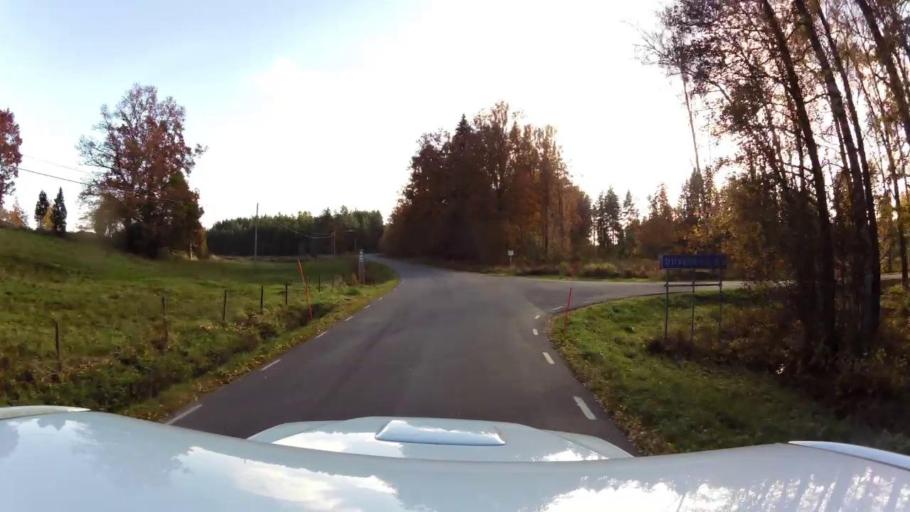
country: SE
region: OEstergoetland
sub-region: Linkopings Kommun
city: Vikingstad
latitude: 58.2732
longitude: 15.4367
